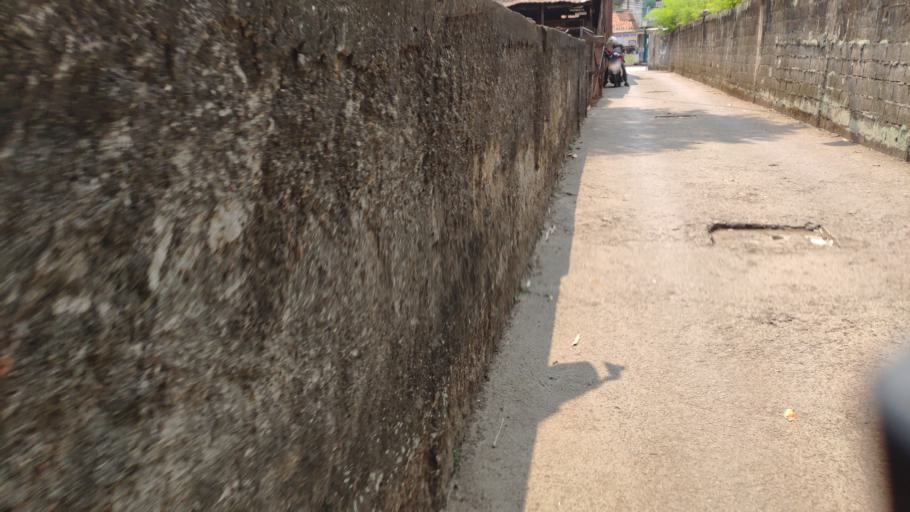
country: ID
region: West Java
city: Pamulang
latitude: -6.3206
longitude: 106.8114
